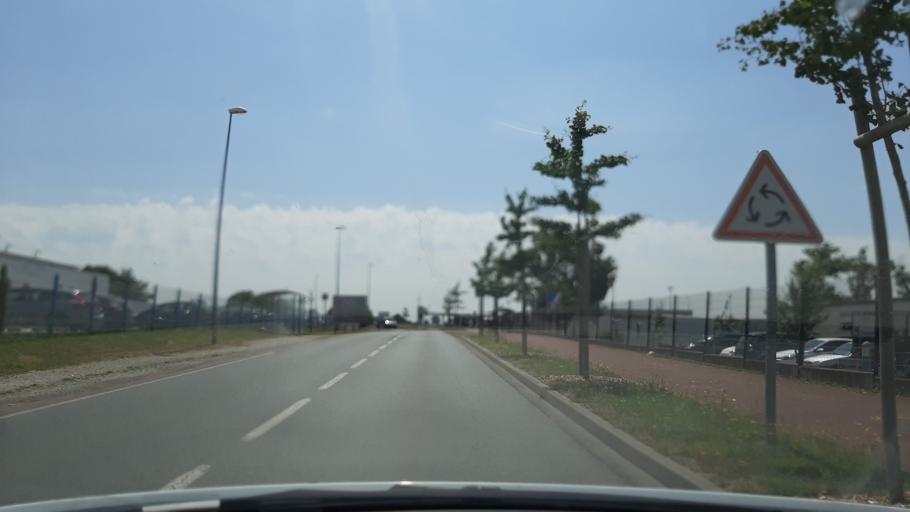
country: FR
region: Pays de la Loire
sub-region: Departement de la Vendee
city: Le Poire-sur-Vie
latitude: 46.7648
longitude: -1.4961
